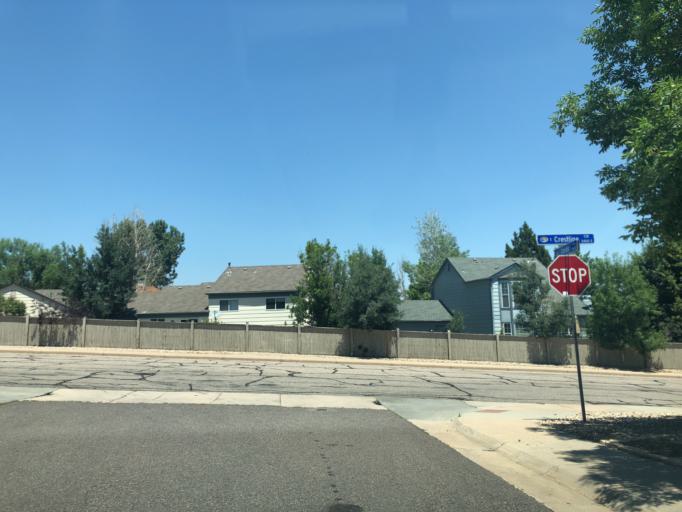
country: US
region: Colorado
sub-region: Arapahoe County
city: Dove Valley
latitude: 39.6180
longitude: -104.7566
